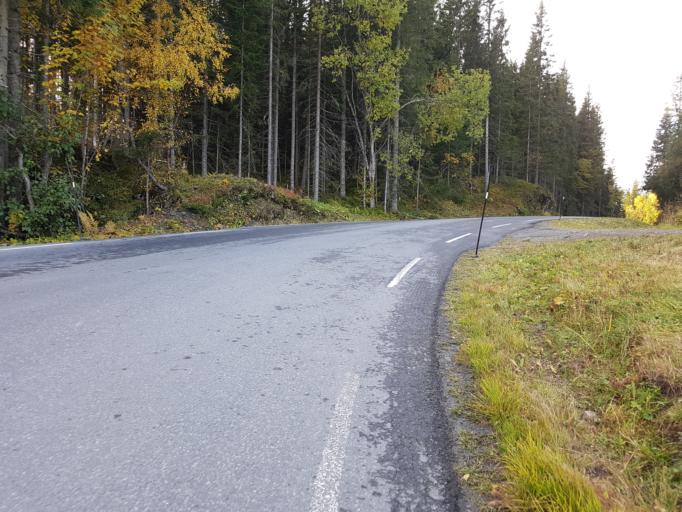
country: NO
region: Sor-Trondelag
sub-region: Klaebu
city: Klaebu
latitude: 63.3460
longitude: 10.5339
